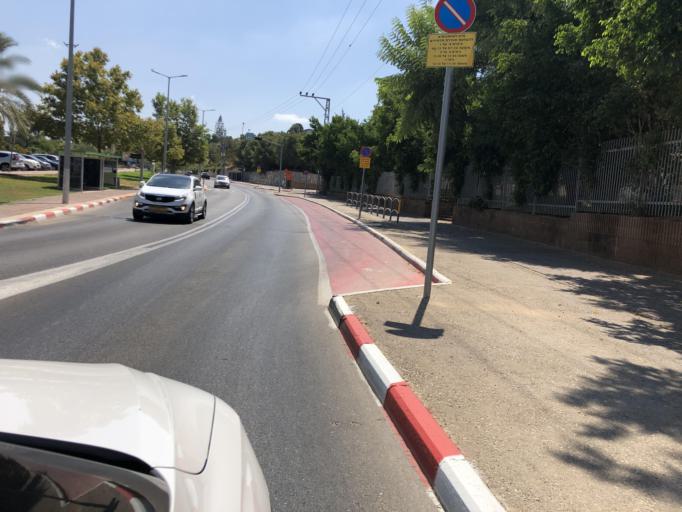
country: IL
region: Central District
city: Rosh Ha'Ayin
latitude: 32.0979
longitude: 34.9589
